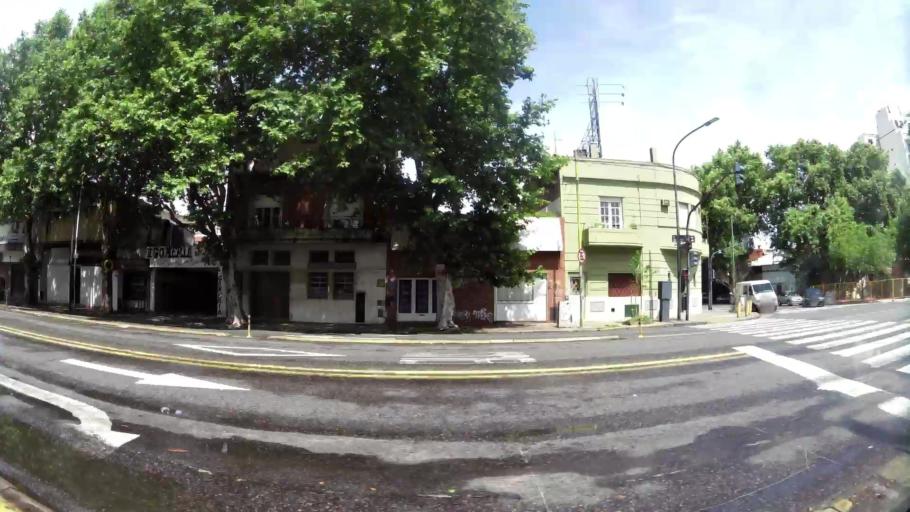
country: AR
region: Buenos Aires F.D.
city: Villa Santa Rita
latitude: -34.6095
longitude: -58.4655
